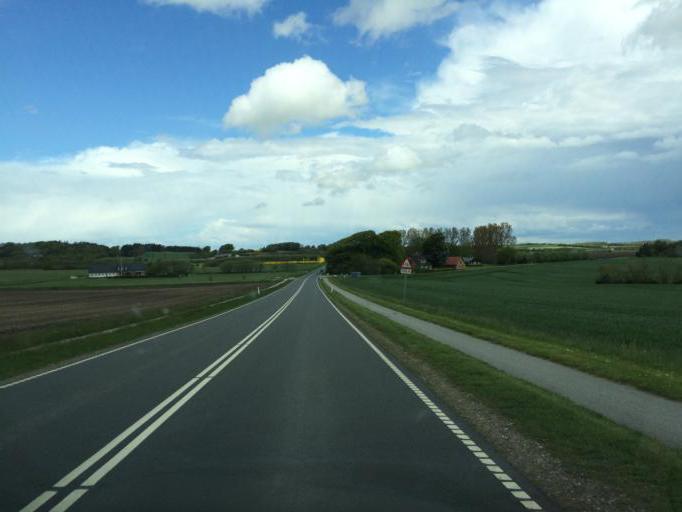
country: DK
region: North Denmark
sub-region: Vesthimmerland Kommune
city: Farso
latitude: 56.7822
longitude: 9.3428
